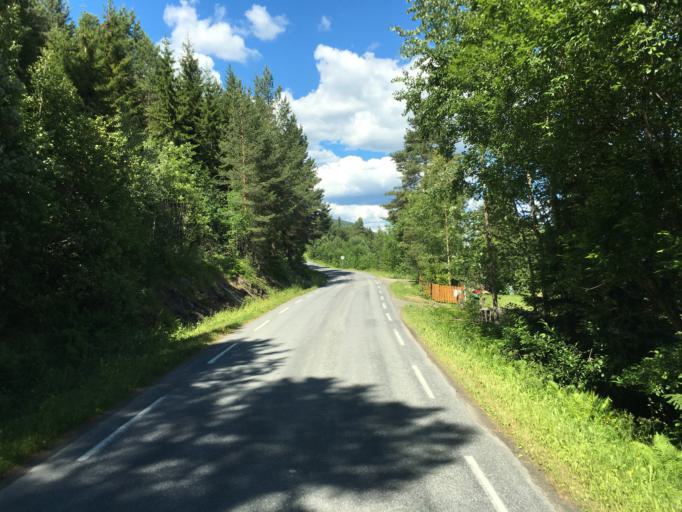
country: NO
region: Oppland
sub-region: Jevnaker
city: Jevnaker
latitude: 60.3153
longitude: 10.3438
